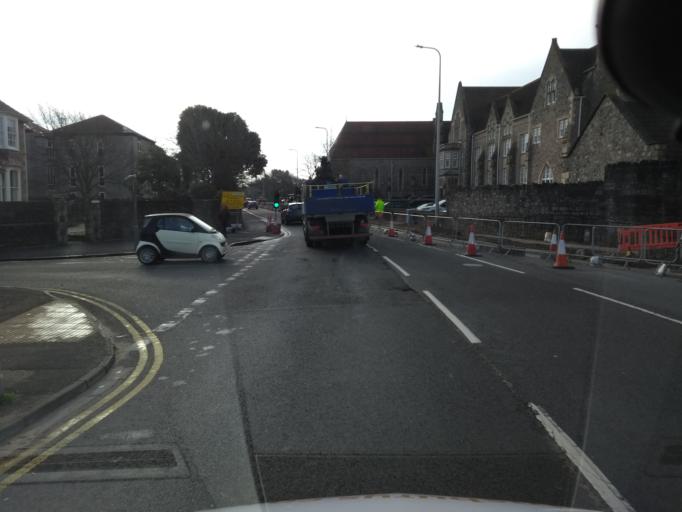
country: GB
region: England
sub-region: North Somerset
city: Weston-super-Mare
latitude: 51.3346
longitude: -2.9825
